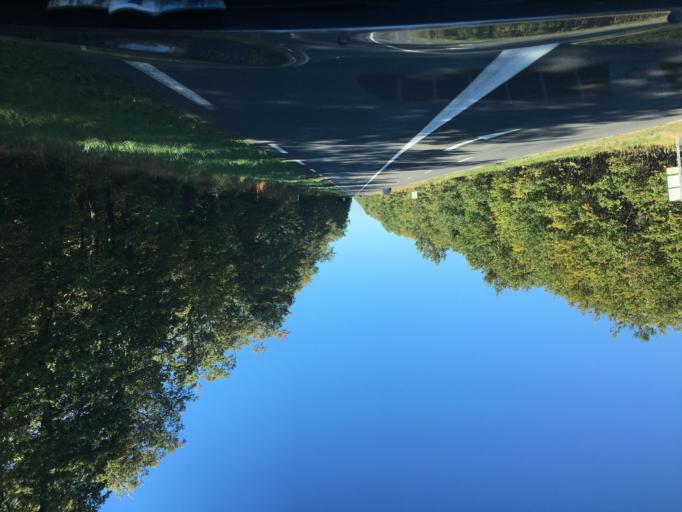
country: FR
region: Centre
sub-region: Departement d'Indre-et-Loire
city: Cheille
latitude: 47.2293
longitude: 0.3962
